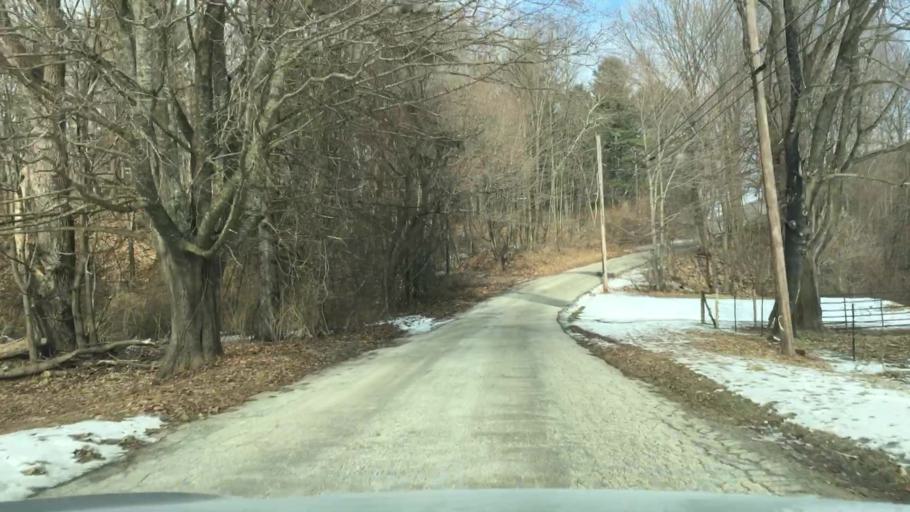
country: US
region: Massachusetts
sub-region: Berkshire County
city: Lee
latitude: 42.3344
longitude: -73.2363
